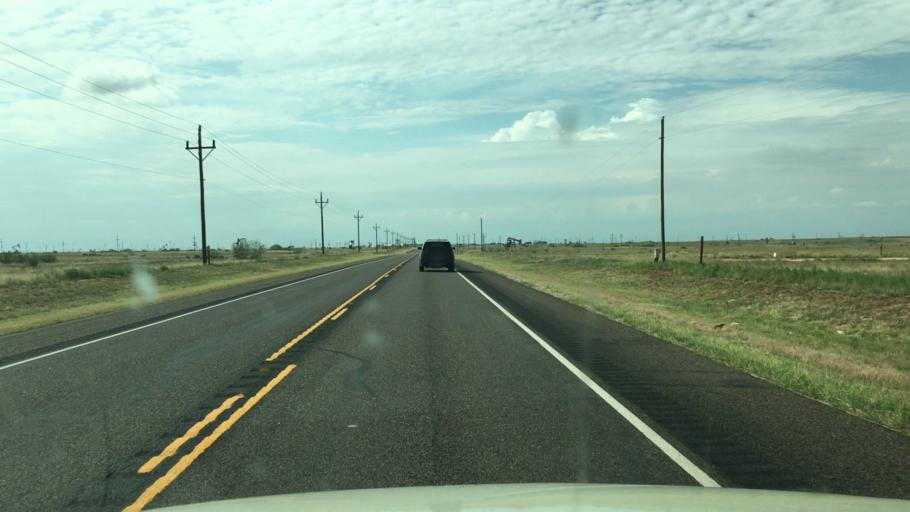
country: US
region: Texas
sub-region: Dawson County
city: Lamesa
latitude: 32.8918
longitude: -102.0912
